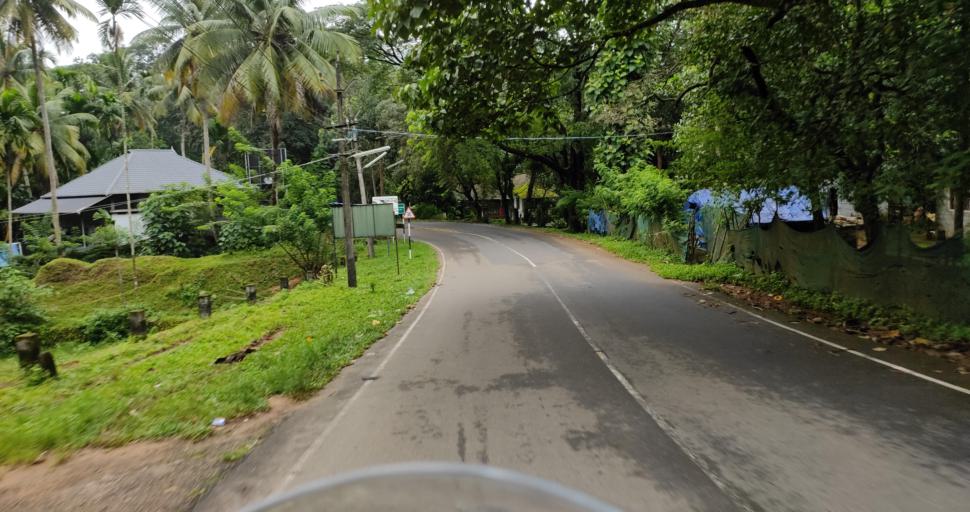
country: IN
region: Kerala
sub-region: Ernakulam
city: Angamali
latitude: 10.2870
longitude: 76.5563
